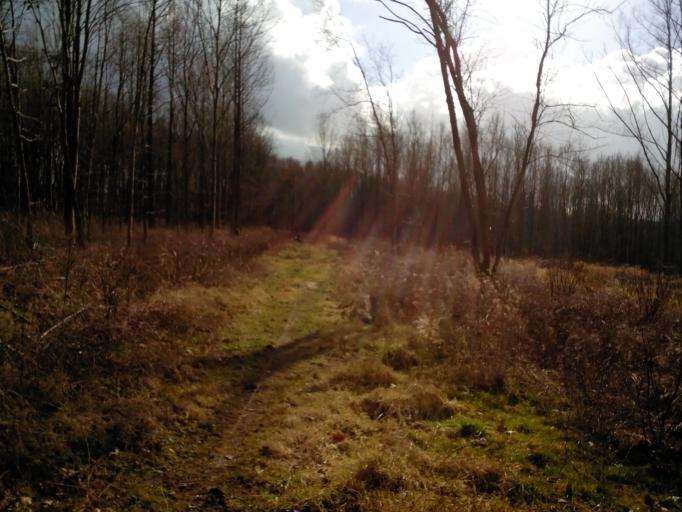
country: BE
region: Flanders
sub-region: Provincie Vlaams-Brabant
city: Oud-Heverlee
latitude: 50.8643
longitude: 4.6702
